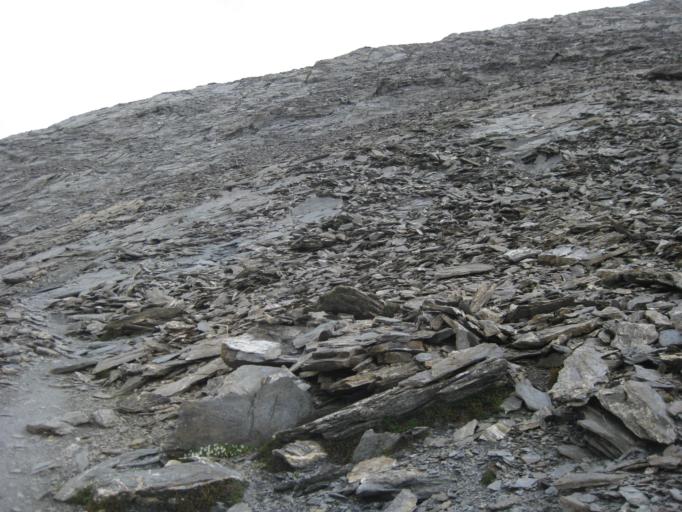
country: IT
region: Piedmont
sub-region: Provincia di Cuneo
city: Pontechianale
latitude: 44.6900
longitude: 6.9919
